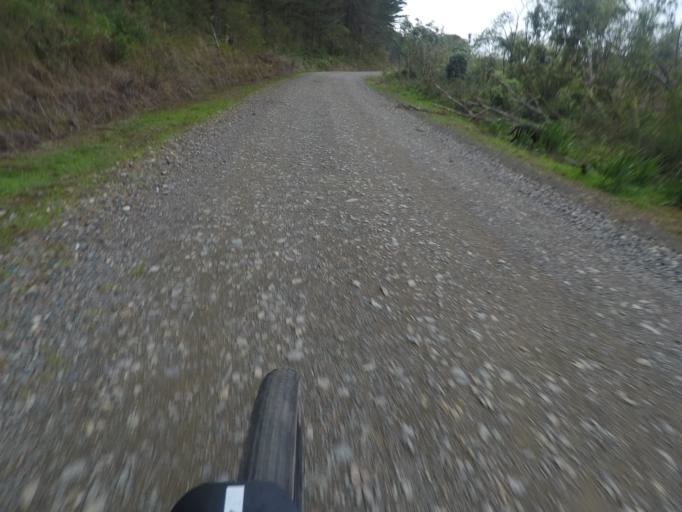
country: NZ
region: Auckland
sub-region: Auckland
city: Muriwai Beach
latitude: -36.7493
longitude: 174.5751
